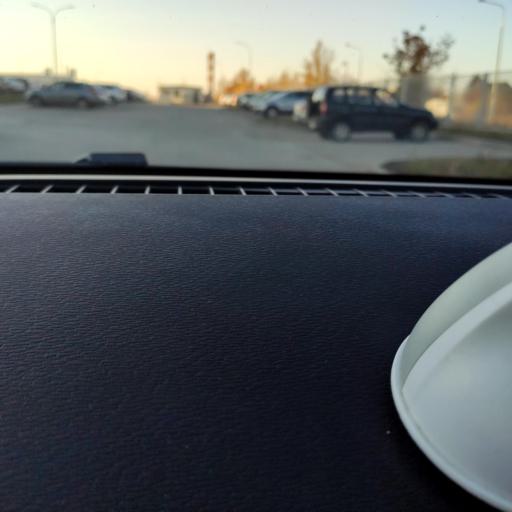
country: RU
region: Samara
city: Petra-Dubrava
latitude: 53.2937
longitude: 50.2414
